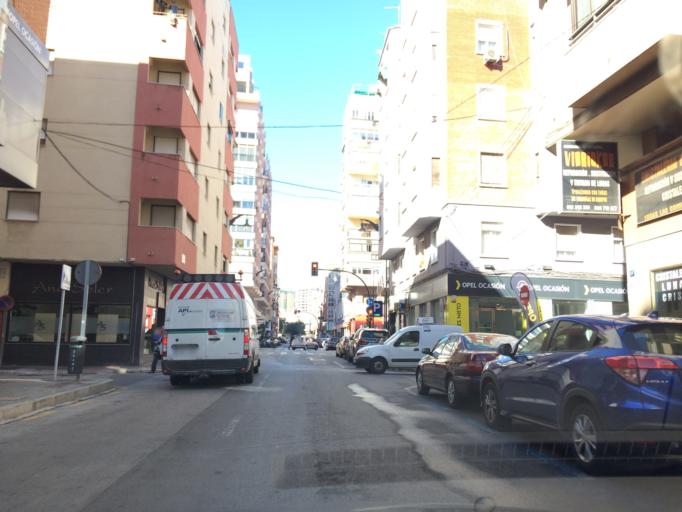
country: ES
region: Andalusia
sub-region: Provincia de Malaga
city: Malaga
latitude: 36.7125
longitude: -4.4275
